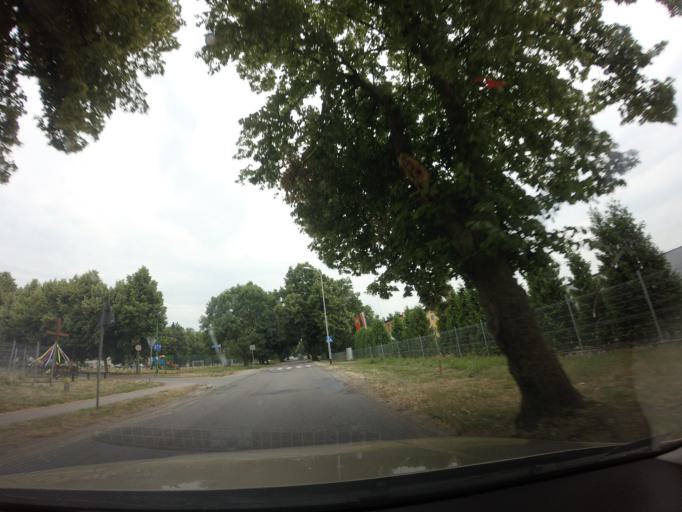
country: PL
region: West Pomeranian Voivodeship
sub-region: Powiat drawski
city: Czaplinek
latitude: 53.5479
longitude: 16.2322
